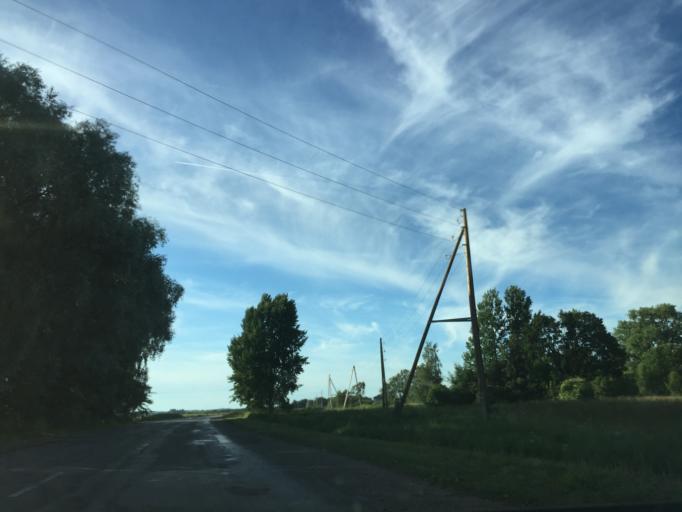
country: LV
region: Ventspils
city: Ventspils
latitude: 57.3072
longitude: 21.5574
